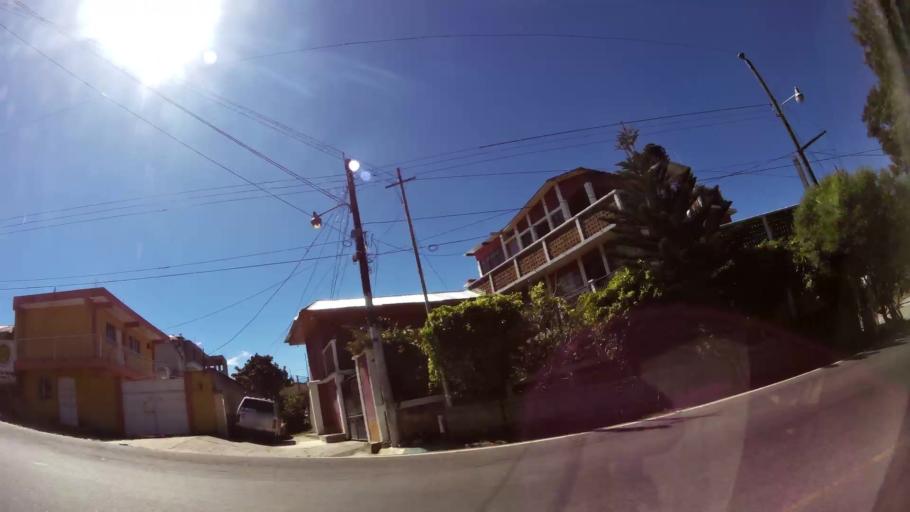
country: GT
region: Solola
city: Solola
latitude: 14.7643
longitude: -91.1775
